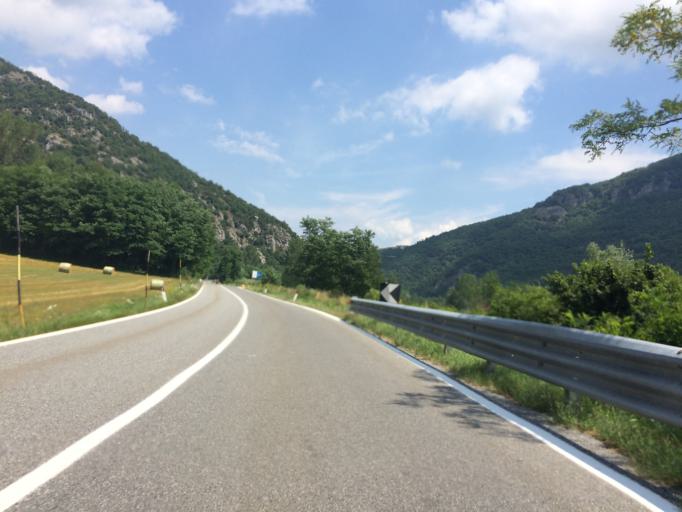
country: IT
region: Piedmont
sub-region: Provincia di Cuneo
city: Priola
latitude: 44.2692
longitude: 8.0294
